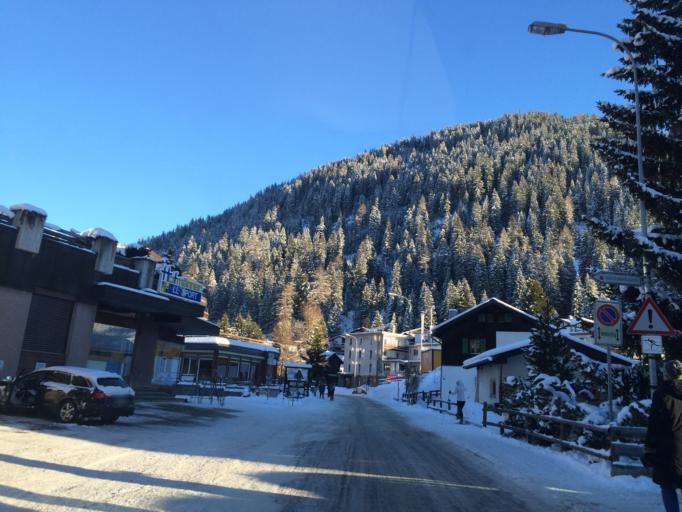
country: CH
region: Grisons
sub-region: Praettigau/Davos District
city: Davos
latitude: 46.7940
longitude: 9.8257
